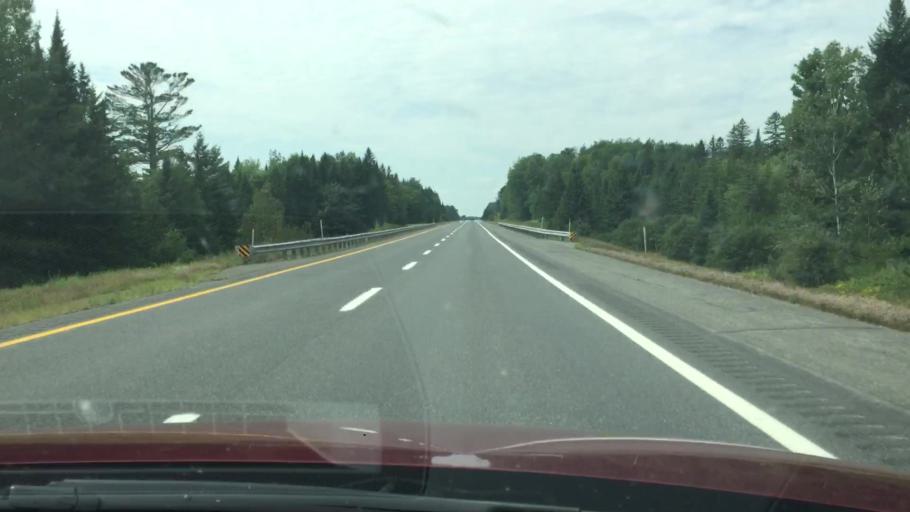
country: US
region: Maine
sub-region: Aroostook County
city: Houlton
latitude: 46.1410
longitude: -67.9853
